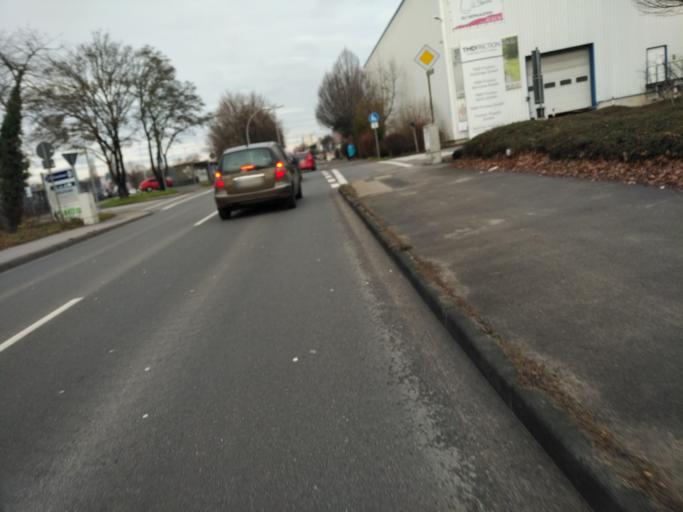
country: DE
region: North Rhine-Westphalia
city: Opladen
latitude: 51.0488
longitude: 7.0162
